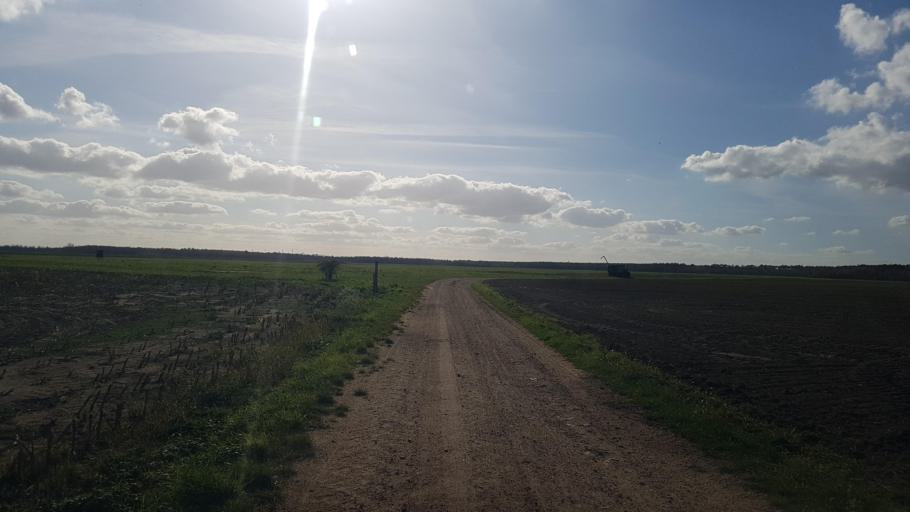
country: DE
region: Saxony
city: Nauwalde
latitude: 51.4469
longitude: 13.3236
